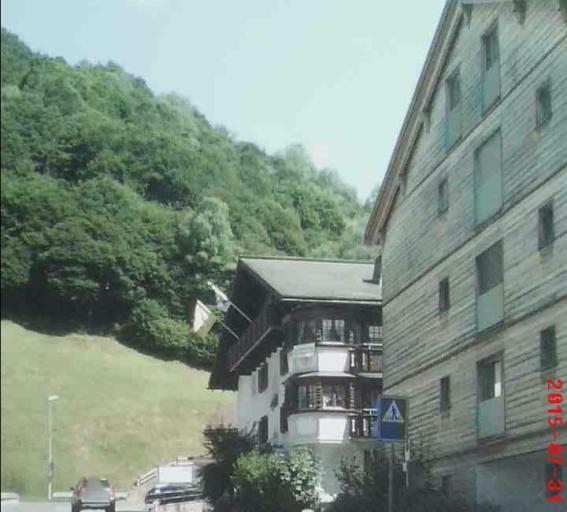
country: CH
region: Grisons
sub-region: Praettigau/Davos District
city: Klosters Serneus
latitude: 46.8830
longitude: 9.8772
